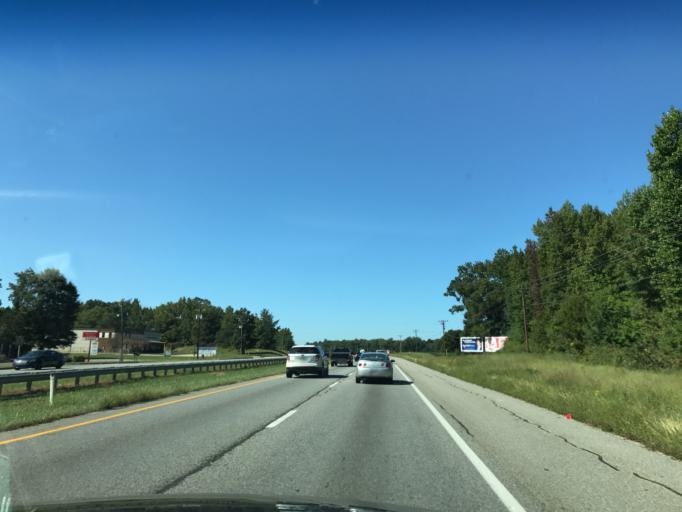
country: US
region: Maryland
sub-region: Charles County
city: Saint Charles
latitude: 38.5803
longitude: -76.9565
